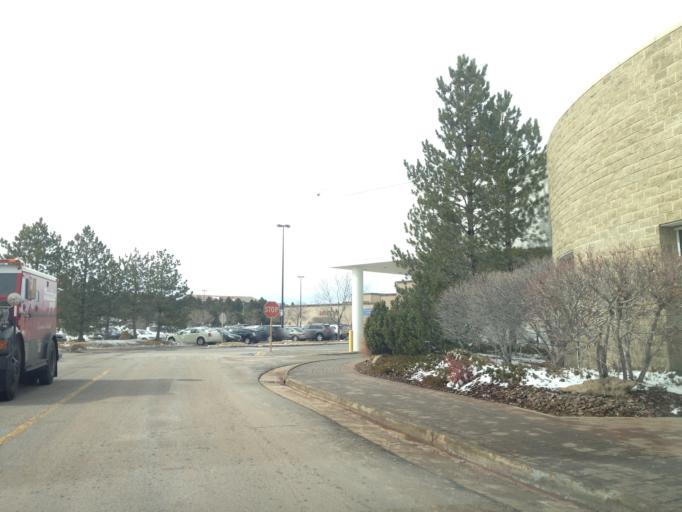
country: US
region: Colorado
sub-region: Boulder County
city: Superior
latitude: 39.9322
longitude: -105.1342
